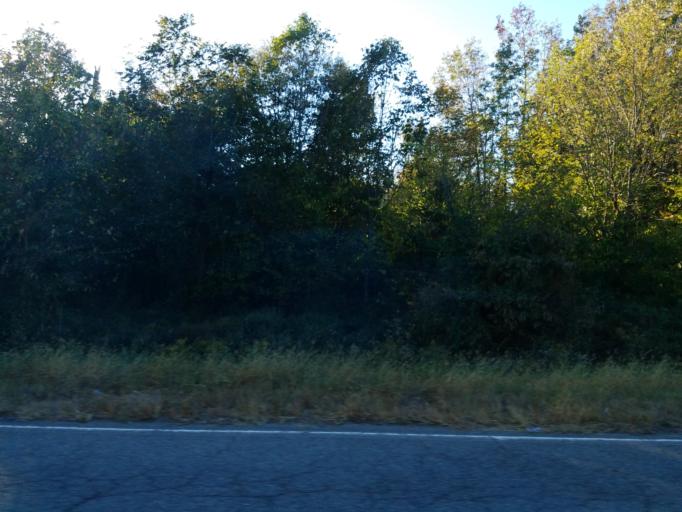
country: US
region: Georgia
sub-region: Bartow County
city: Adairsville
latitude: 34.3086
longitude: -84.9377
